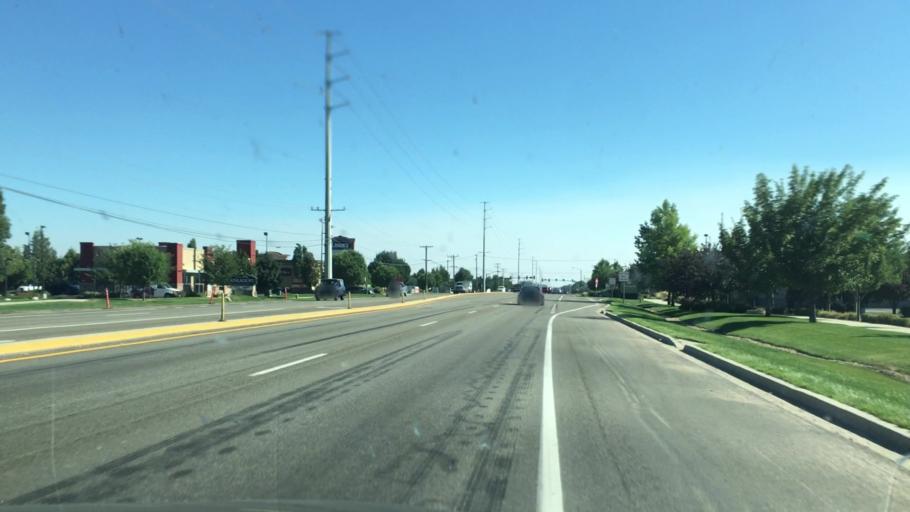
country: US
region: Idaho
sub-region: Ada County
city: Meridian
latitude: 43.6372
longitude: -116.3544
